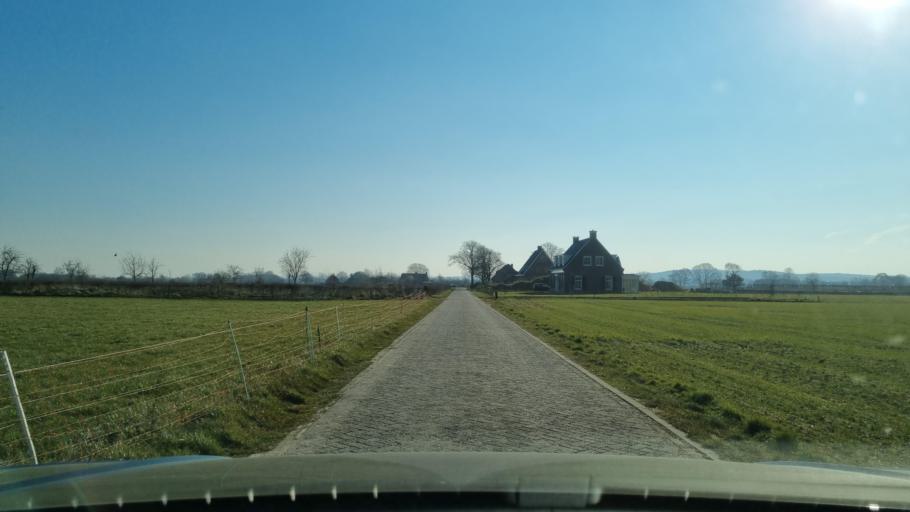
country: NL
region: Gelderland
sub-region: Gemeente Groesbeek
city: De Horst
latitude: 51.7859
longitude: 5.9536
